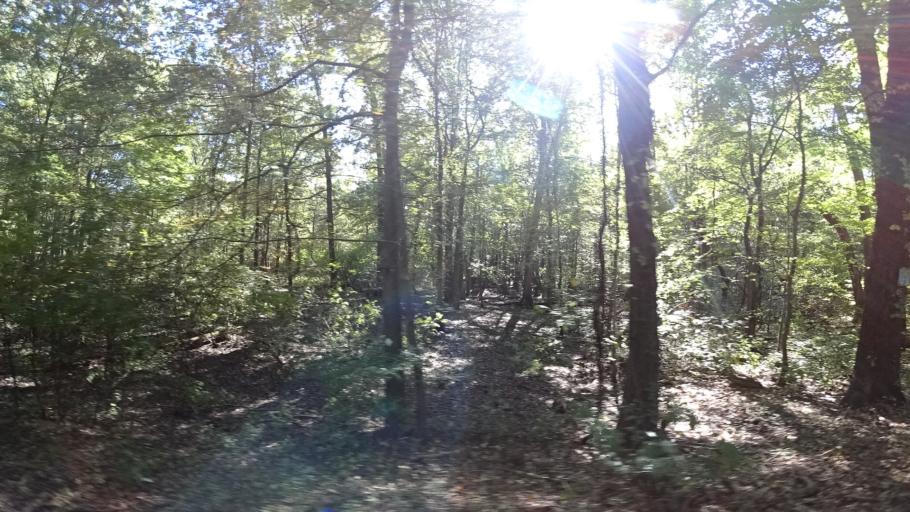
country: US
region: Indiana
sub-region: LaPorte County
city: Long Beach
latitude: 41.7455
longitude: -86.8212
